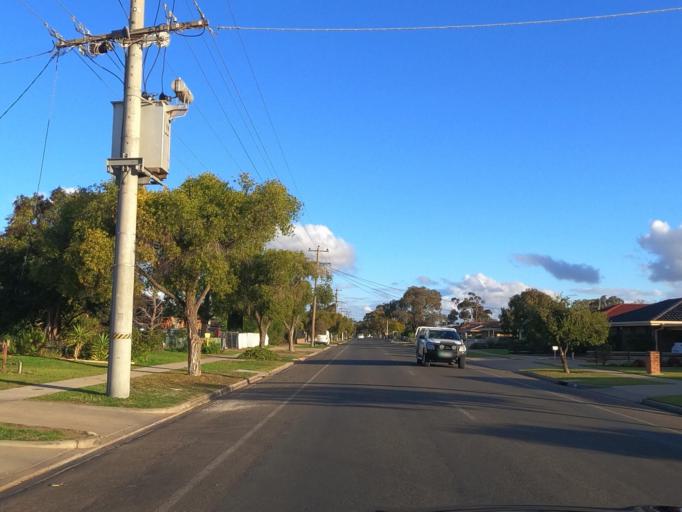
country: AU
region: Victoria
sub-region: Swan Hill
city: Swan Hill
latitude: -35.3419
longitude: 143.5439
